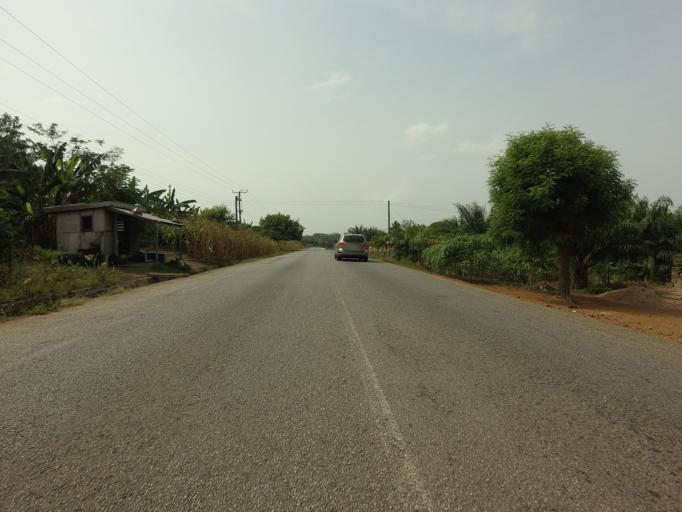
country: GH
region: Volta
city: Ho
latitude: 6.3433
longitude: 0.1737
